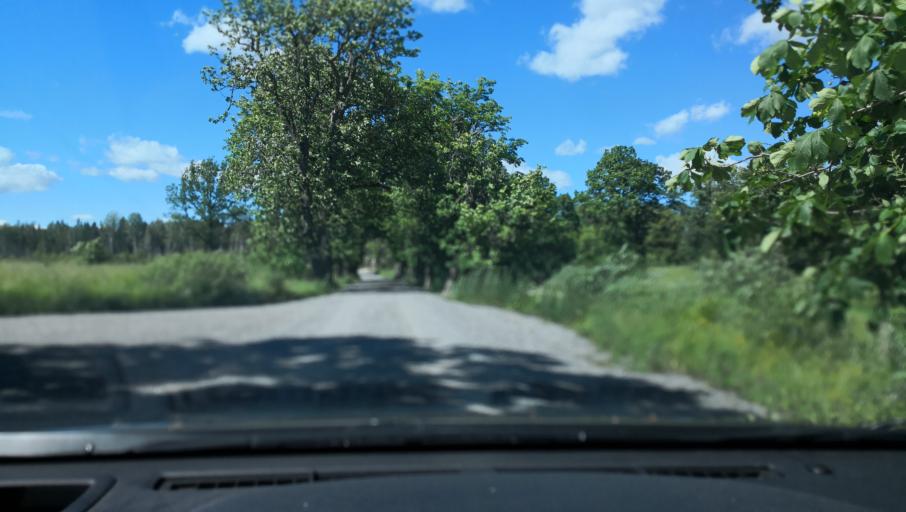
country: SE
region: Soedermanland
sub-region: Eskilstuna Kommun
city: Hallbybrunn
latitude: 59.3008
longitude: 16.3611
